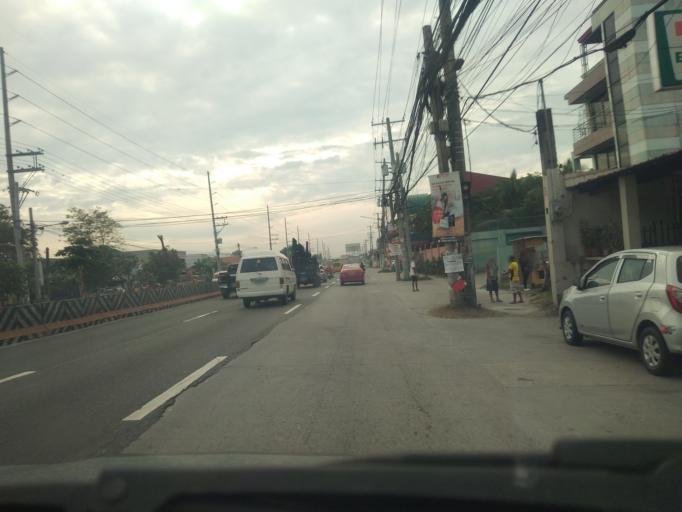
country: PH
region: Central Luzon
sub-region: Province of Pampanga
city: Magliman
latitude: 15.0525
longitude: 120.6627
